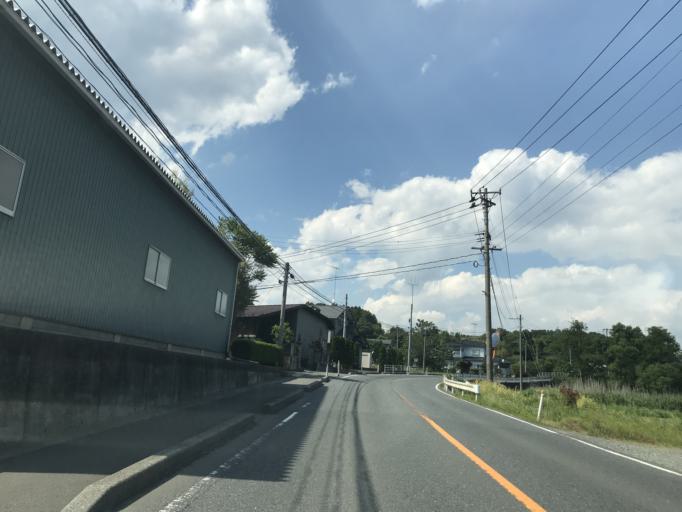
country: JP
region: Miyagi
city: Wakuya
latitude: 38.4880
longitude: 141.1076
